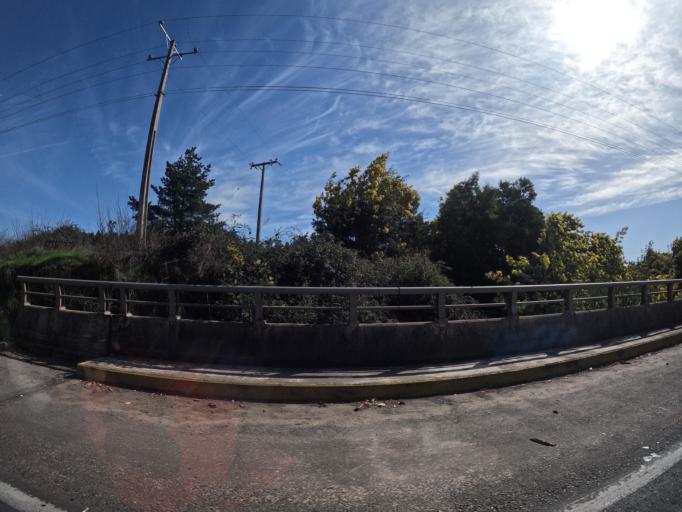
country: CL
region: Biobio
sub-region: Provincia de Biobio
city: Cabrero
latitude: -36.9449
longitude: -72.3498
